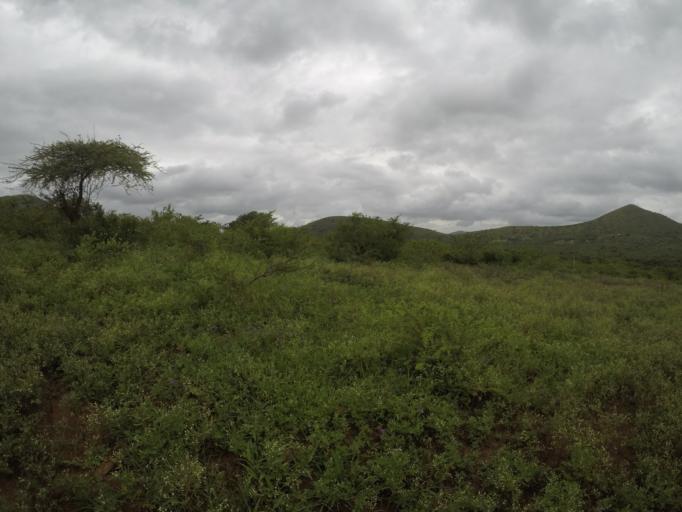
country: ZA
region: KwaZulu-Natal
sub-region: uThungulu District Municipality
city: Empangeni
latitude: -28.5893
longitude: 31.8607
